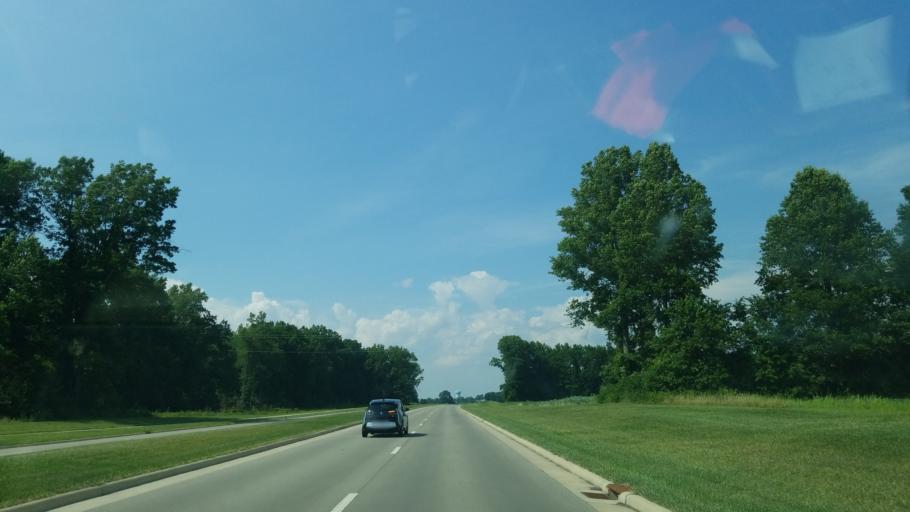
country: US
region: Ohio
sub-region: Delaware County
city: Delaware
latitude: 40.2568
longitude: -83.0912
